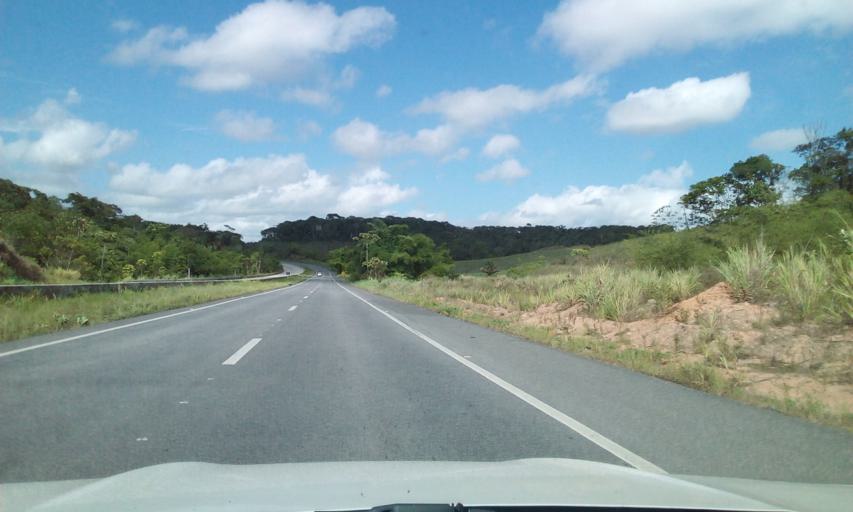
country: BR
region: Alagoas
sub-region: Rio Largo
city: Rio Largo
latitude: -9.5014
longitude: -35.9059
